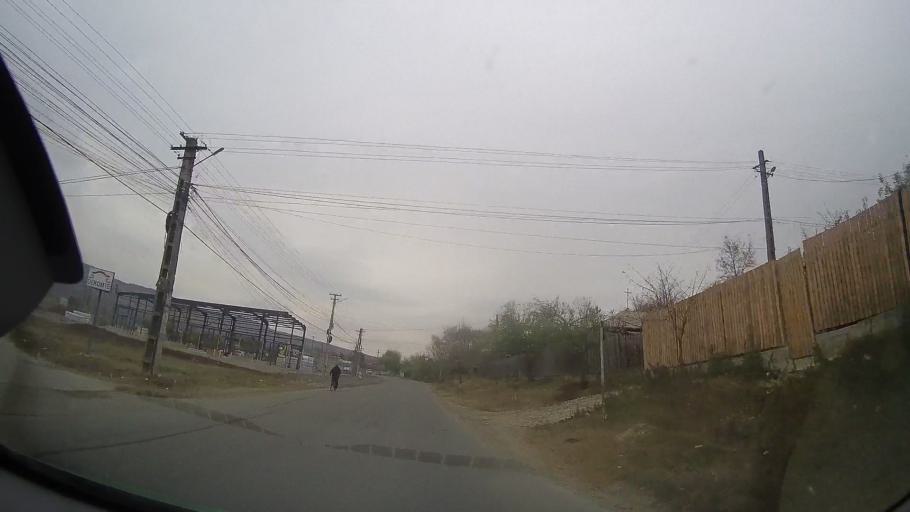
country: RO
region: Prahova
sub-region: Oras Urlati
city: Urlati
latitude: 44.9994
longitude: 26.2281
